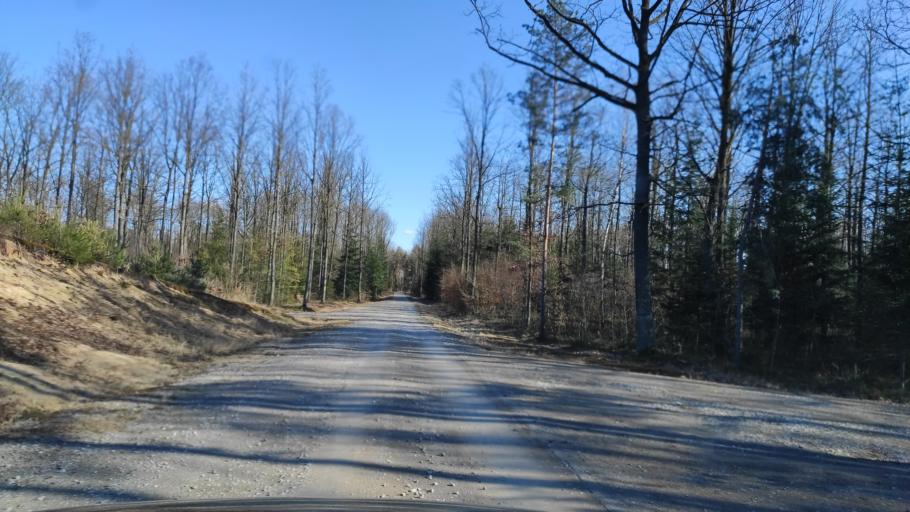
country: PL
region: Masovian Voivodeship
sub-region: Powiat radomski
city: Jedlnia-Letnisko
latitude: 51.4496
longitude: 21.2907
